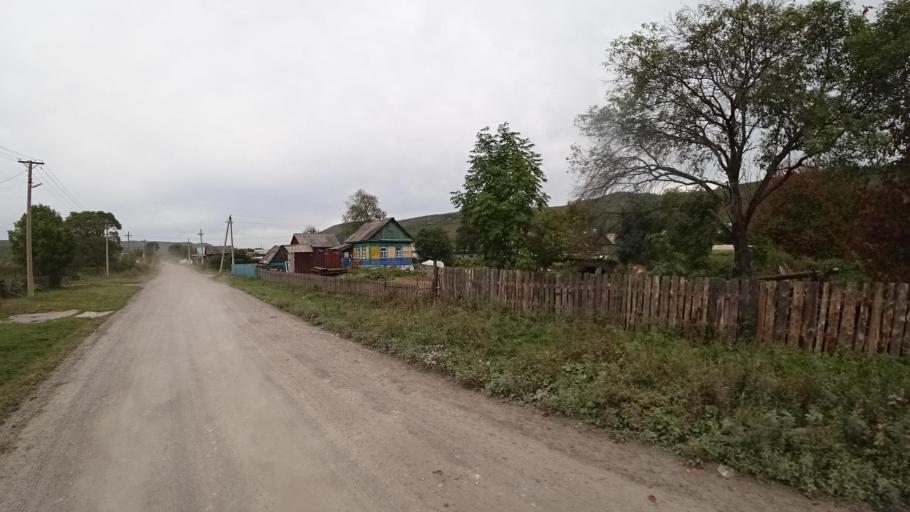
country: RU
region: Jewish Autonomous Oblast
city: Khingansk
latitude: 49.0347
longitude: 131.0494
